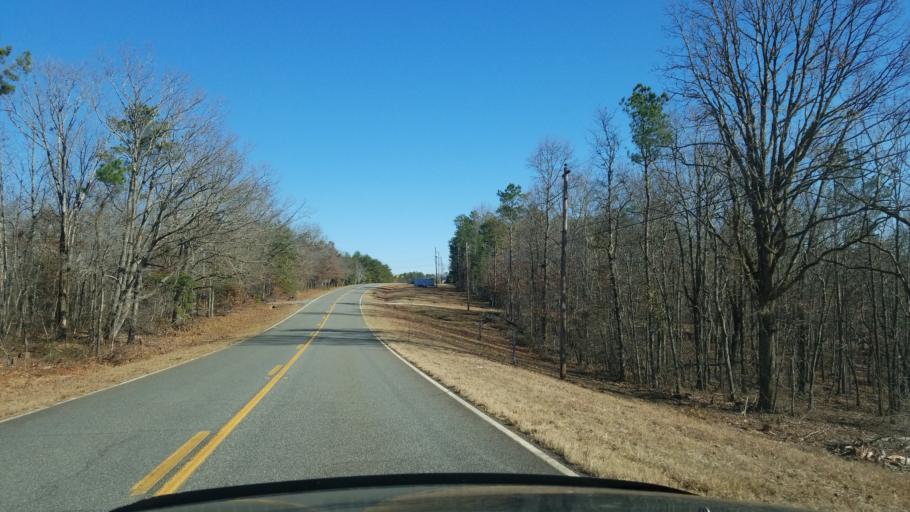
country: US
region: Georgia
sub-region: Meriwether County
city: Manchester
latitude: 32.8426
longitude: -84.6684
